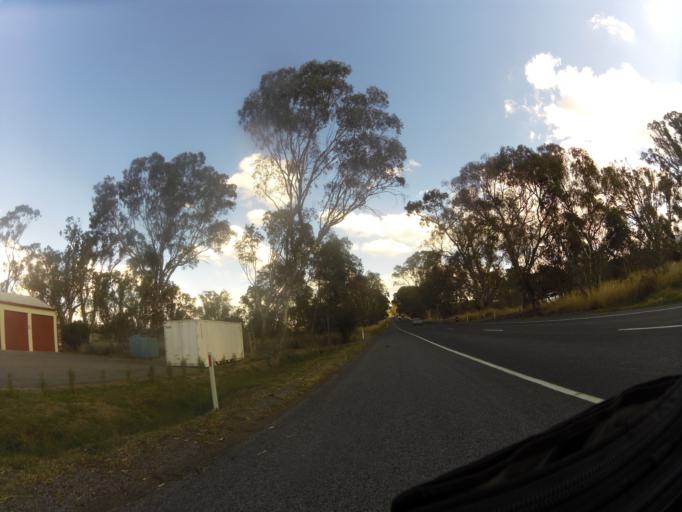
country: AU
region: Victoria
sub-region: Mansfield
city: Mansfield
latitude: -36.9340
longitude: 145.9999
